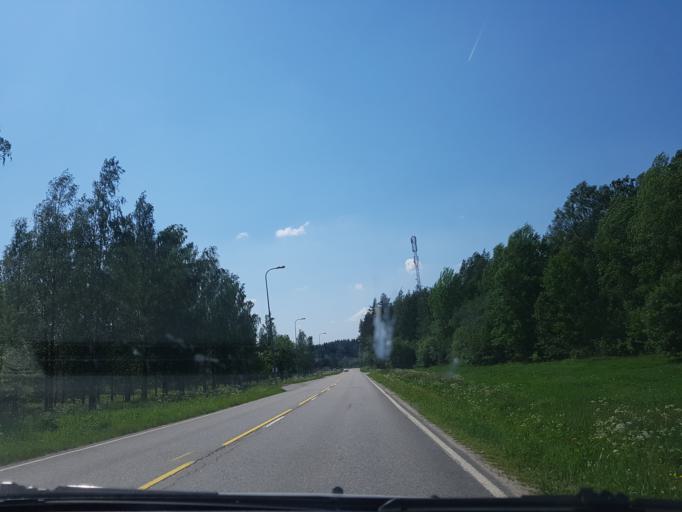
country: FI
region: Uusimaa
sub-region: Helsinki
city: Vihti
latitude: 60.3309
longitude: 24.4241
